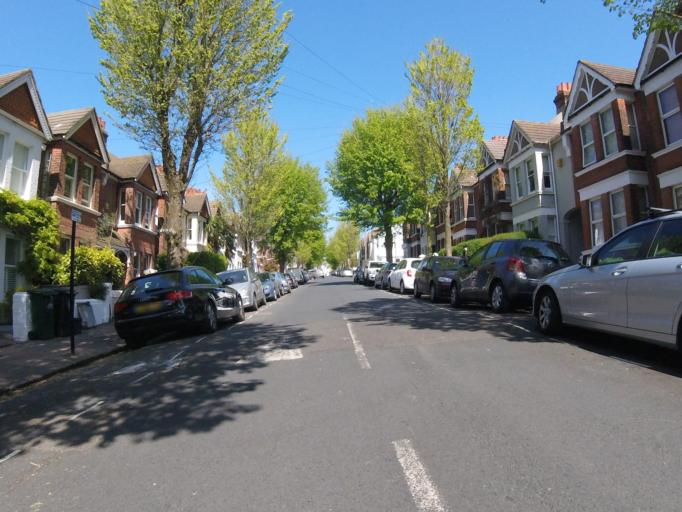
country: GB
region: England
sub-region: Brighton and Hove
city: Brighton
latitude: 50.8455
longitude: -0.1391
